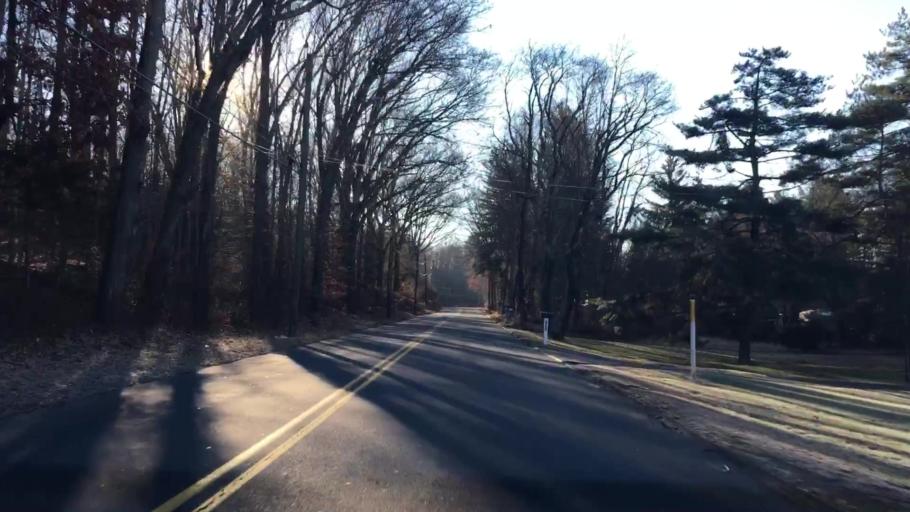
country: US
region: Connecticut
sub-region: New Haven County
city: Cheshire Village
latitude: 41.5593
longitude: -72.8718
